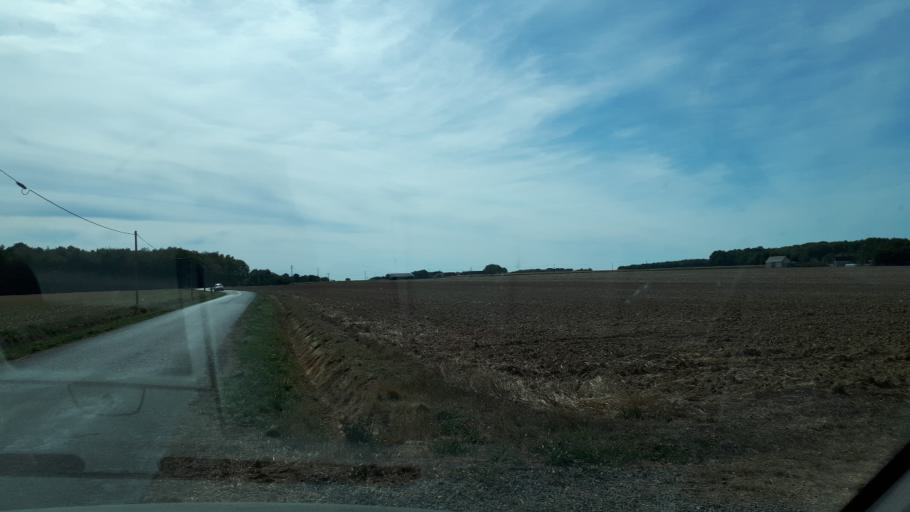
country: FR
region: Centre
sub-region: Departement du Loir-et-Cher
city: Montoire-sur-le-Loir
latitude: 47.6989
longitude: 0.8319
